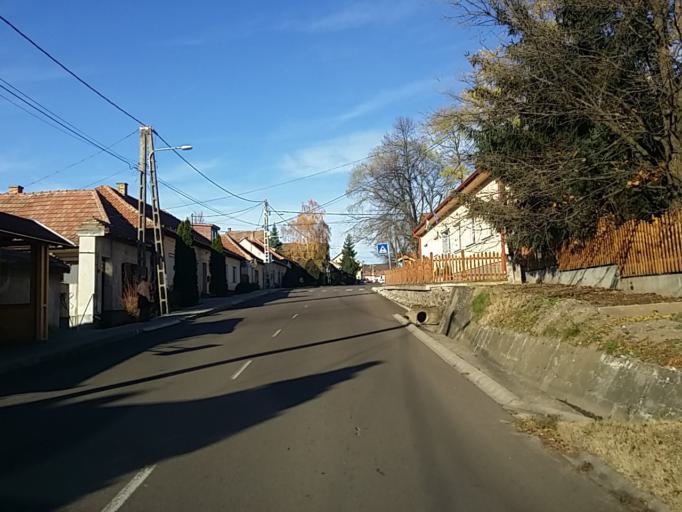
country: HU
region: Heves
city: Abasar
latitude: 47.8152
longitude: 19.9941
